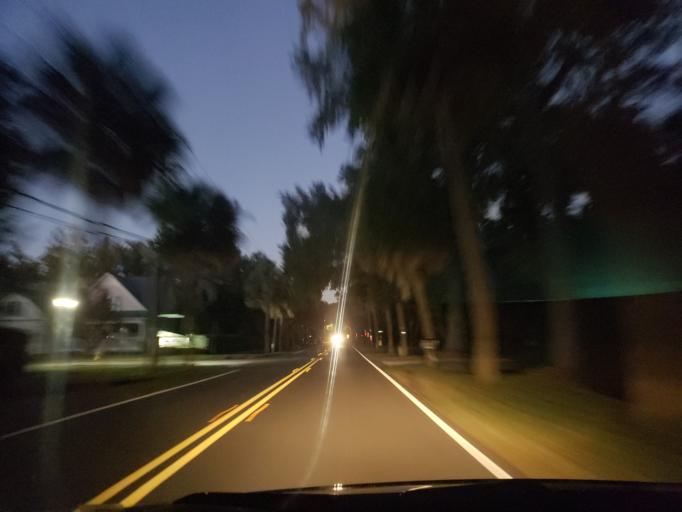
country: US
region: Georgia
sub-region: Chatham County
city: Isle of Hope
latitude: 31.9917
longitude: -81.0675
